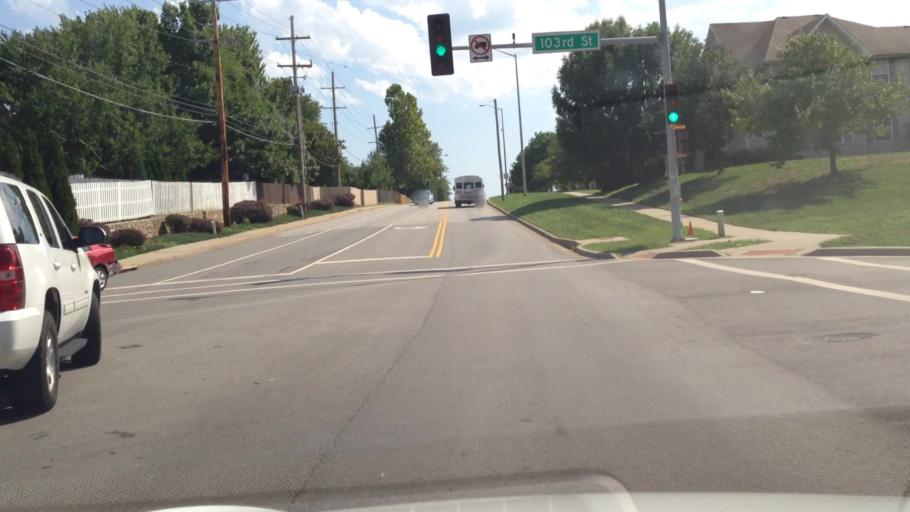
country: US
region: Kansas
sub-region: Johnson County
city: Lenexa
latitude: 38.9421
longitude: -94.7422
